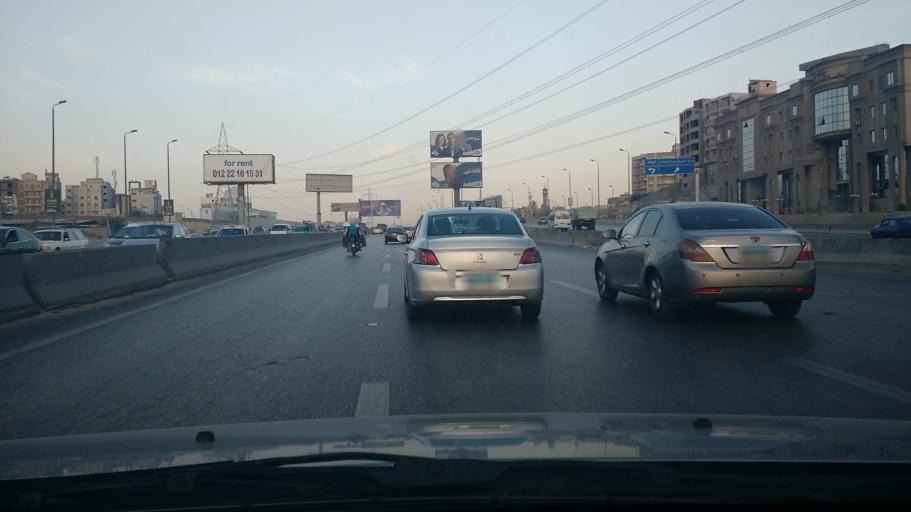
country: EG
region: Muhafazat al Qahirah
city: Cairo
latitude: 29.9881
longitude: 31.3035
